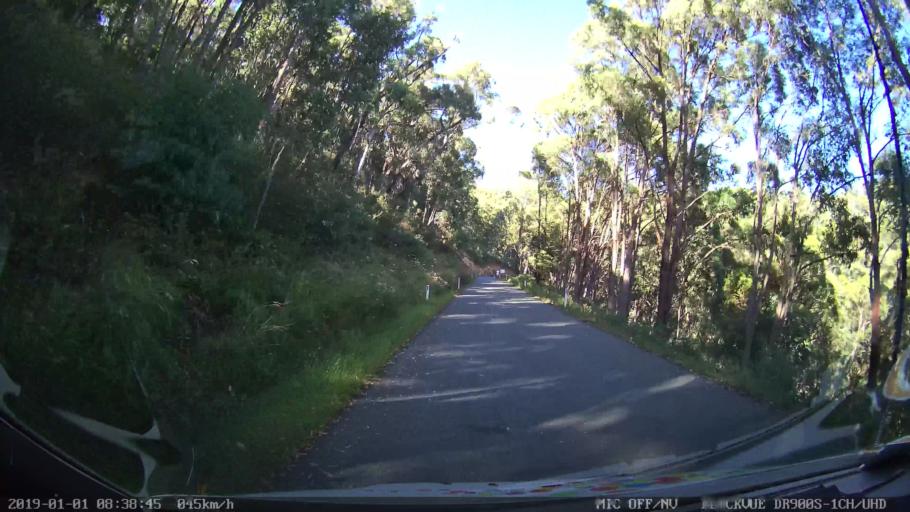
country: AU
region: New South Wales
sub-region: Snowy River
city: Jindabyne
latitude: -36.3323
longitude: 148.1962
